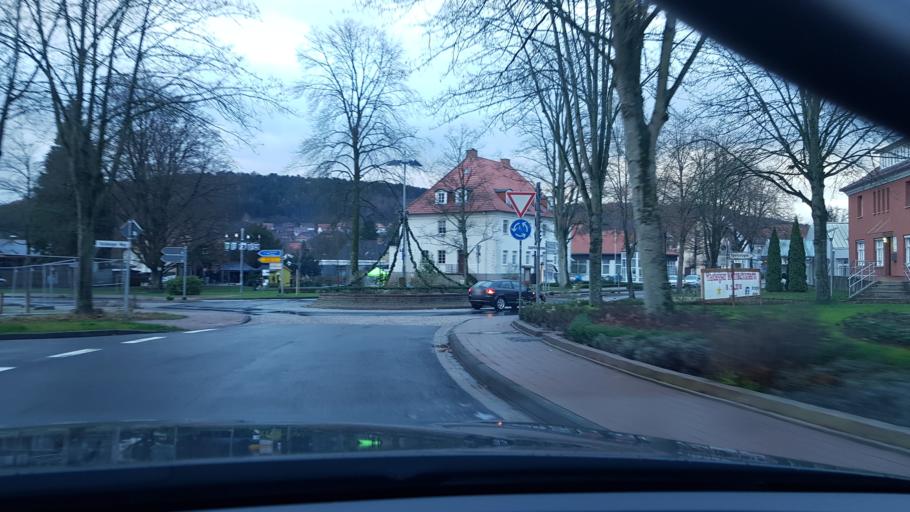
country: DE
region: Lower Saxony
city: Hardegsen
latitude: 51.6535
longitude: 9.8321
